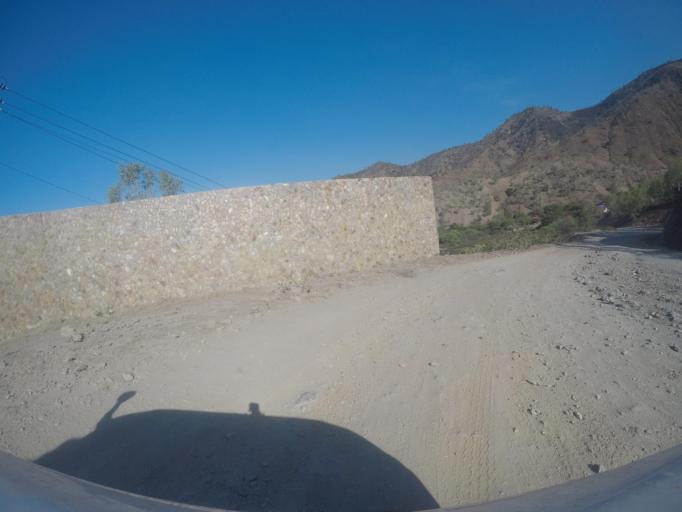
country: TL
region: Dili
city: Dili
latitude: -8.5266
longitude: 125.6306
